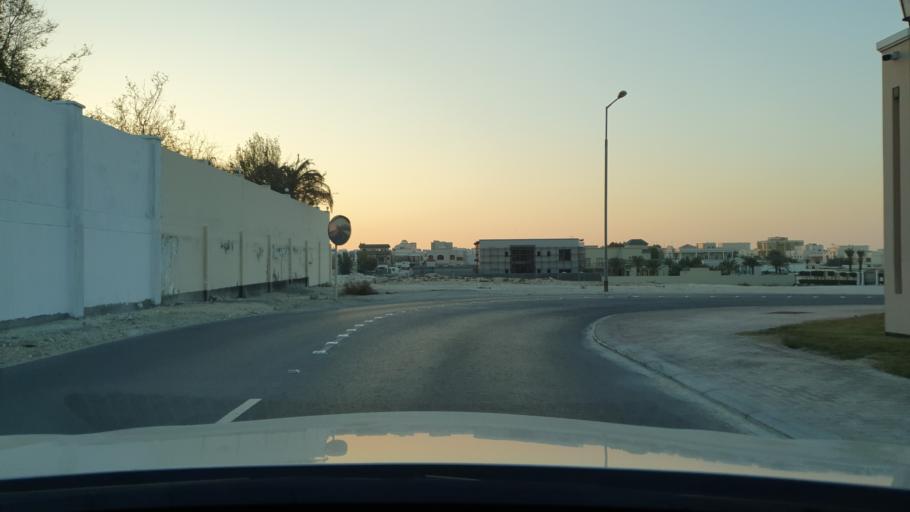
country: BH
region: Northern
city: Ar Rifa'
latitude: 26.1404
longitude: 50.5316
